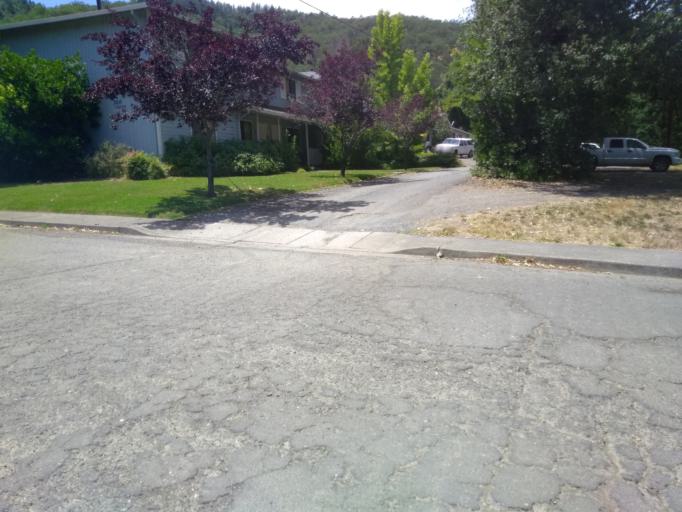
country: US
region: California
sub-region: Mendocino County
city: Ukiah
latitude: 39.1289
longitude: -123.2115
